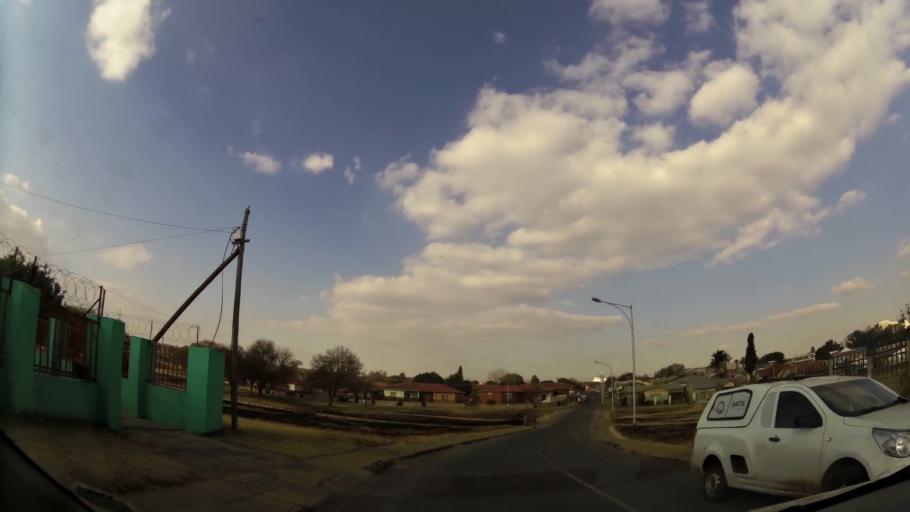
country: ZA
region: Gauteng
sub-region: West Rand District Municipality
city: Krugersdorp
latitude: -26.0964
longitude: 27.7531
